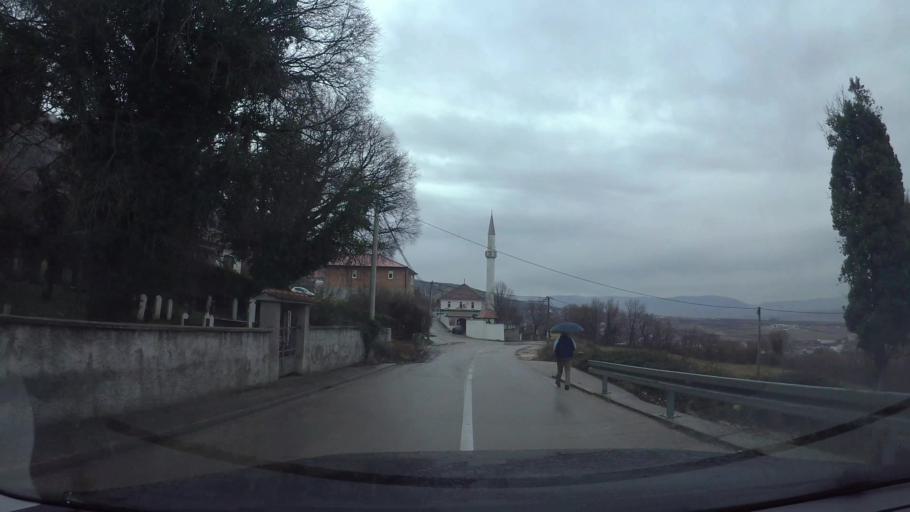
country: BA
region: Federation of Bosnia and Herzegovina
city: Blagaj
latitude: 43.2944
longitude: 17.8571
